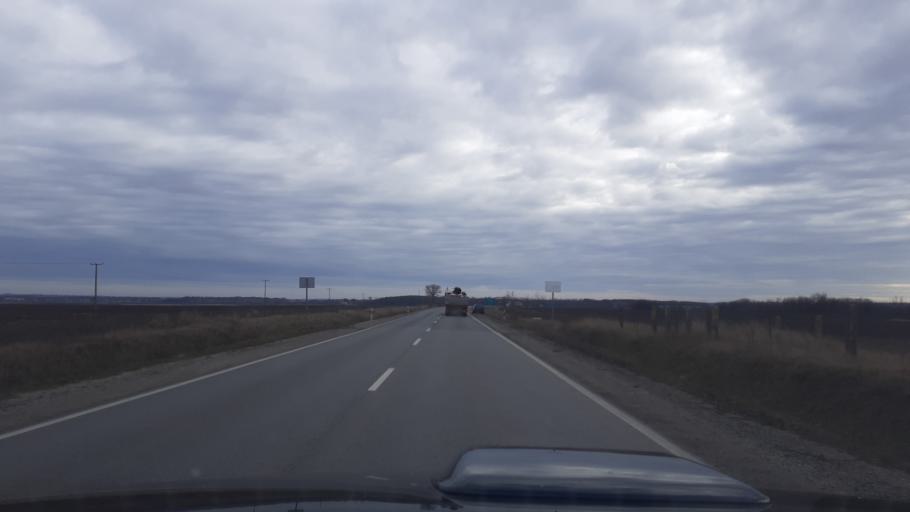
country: HU
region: Fejer
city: Seregelyes
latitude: 47.1341
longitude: 18.5423
